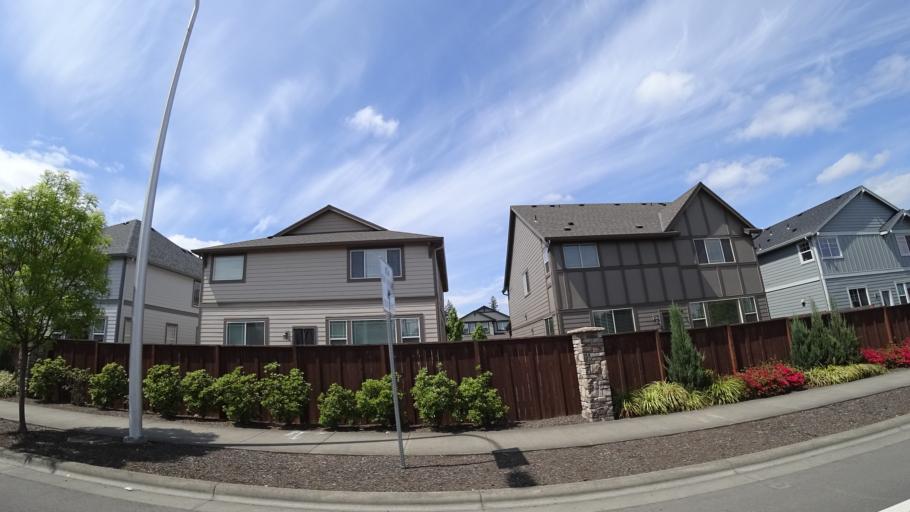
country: US
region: Oregon
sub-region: Washington County
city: Rockcreek
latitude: 45.5245
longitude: -122.9001
